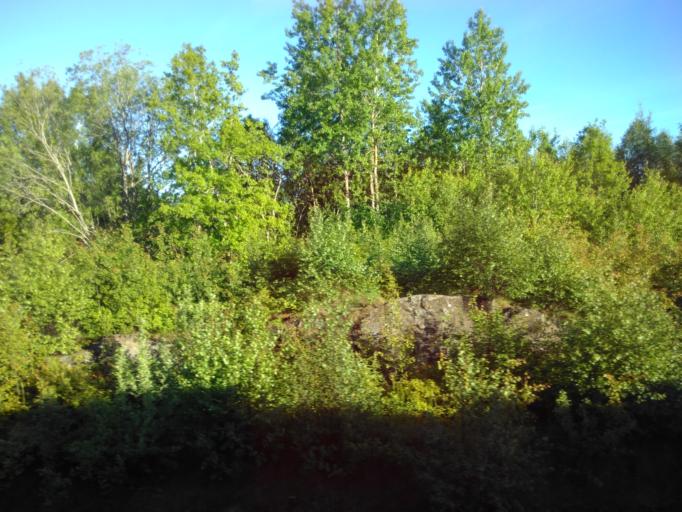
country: SE
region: Soedermanland
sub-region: Flens Kommun
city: Flen
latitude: 59.0539
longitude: 16.5698
